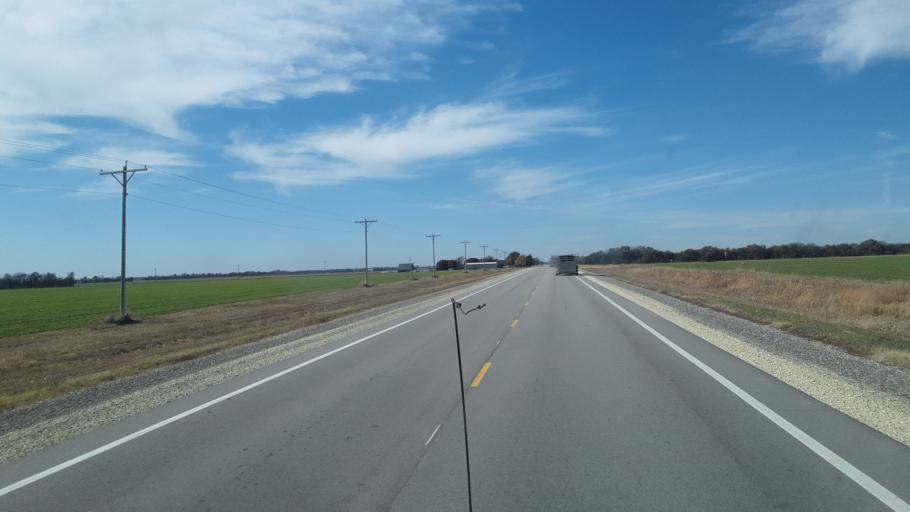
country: US
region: Kansas
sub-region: McPherson County
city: McPherson
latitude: 38.3771
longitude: -97.5214
